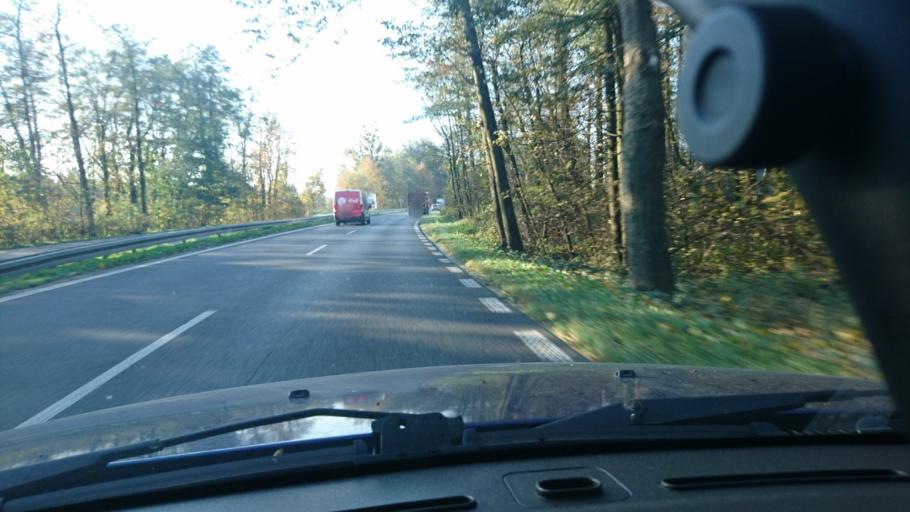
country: PL
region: Silesian Voivodeship
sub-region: Powiat cieszynski
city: Gorki Wielkie
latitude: 49.7645
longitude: 18.8092
